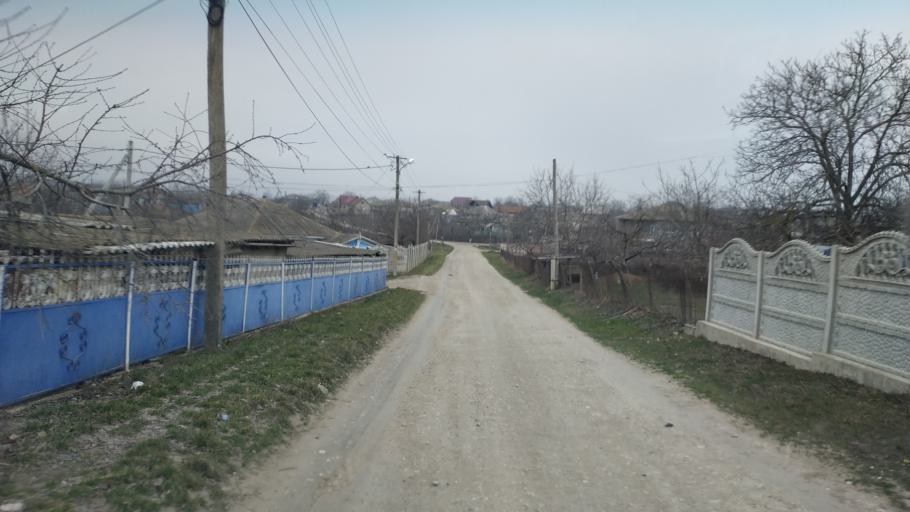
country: MD
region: Chisinau
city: Singera
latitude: 46.8249
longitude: 29.0267
